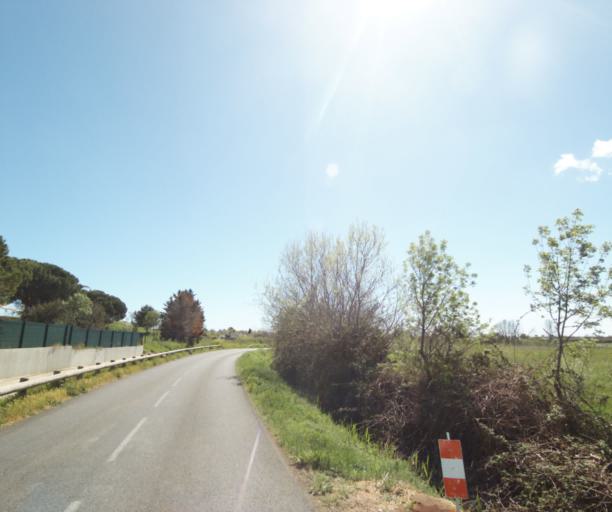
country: FR
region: Languedoc-Roussillon
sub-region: Departement de l'Herault
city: Lattes
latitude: 43.5628
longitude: 3.9216
